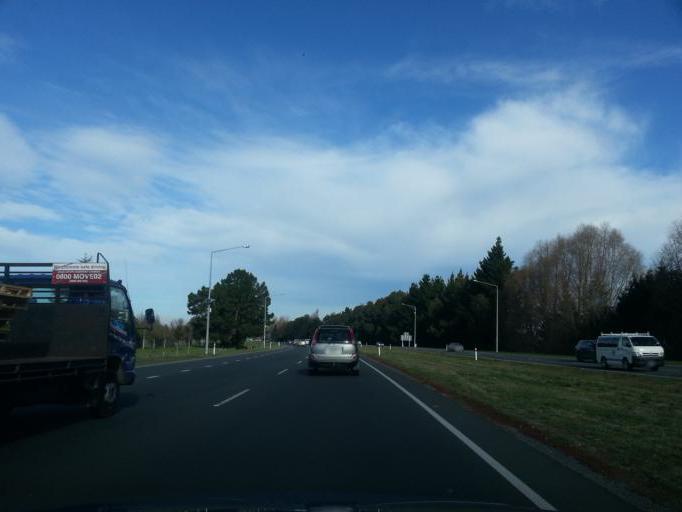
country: NZ
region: Canterbury
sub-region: Waimakariri District
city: Kaiapoi
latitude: -43.3900
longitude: 172.6400
